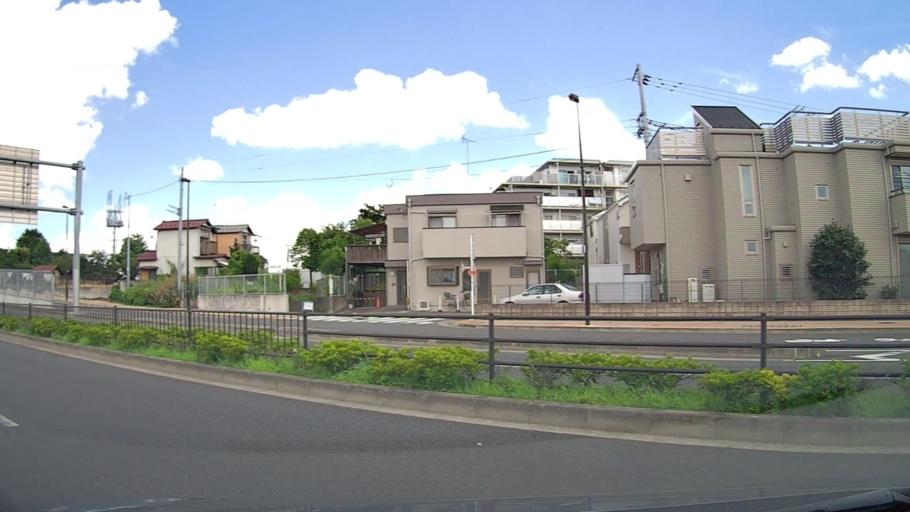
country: JP
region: Tokyo
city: Nishi-Tokyo-shi
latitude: 35.7450
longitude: 139.5580
